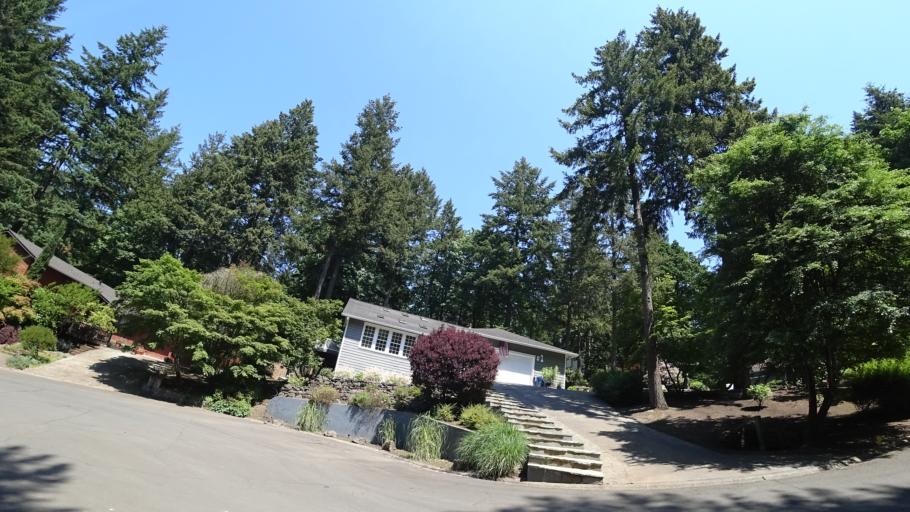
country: US
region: Oregon
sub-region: Washington County
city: Metzger
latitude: 45.4311
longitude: -122.7224
